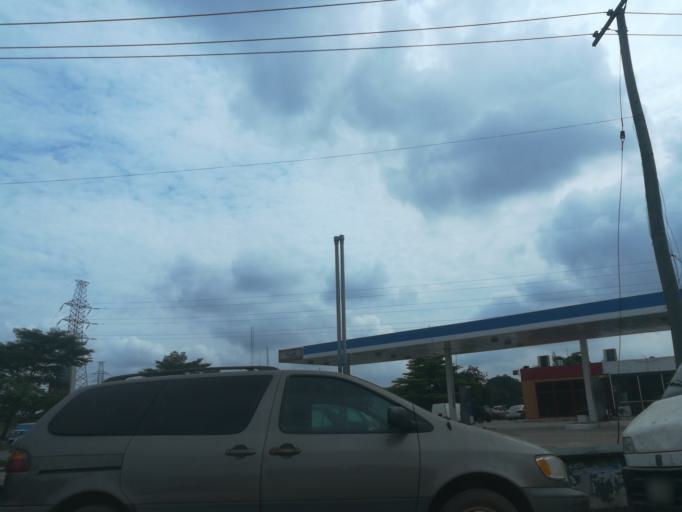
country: NG
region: Lagos
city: Somolu
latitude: 6.5484
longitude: 3.3885
